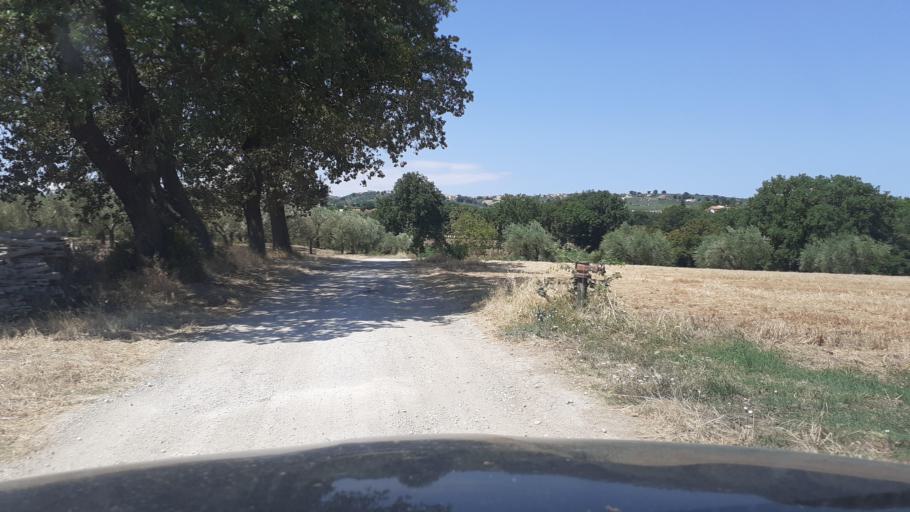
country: IT
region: Abruzzo
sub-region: Provincia di Chieti
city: Santa Maria Imbaro
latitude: 42.2071
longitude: 14.4786
